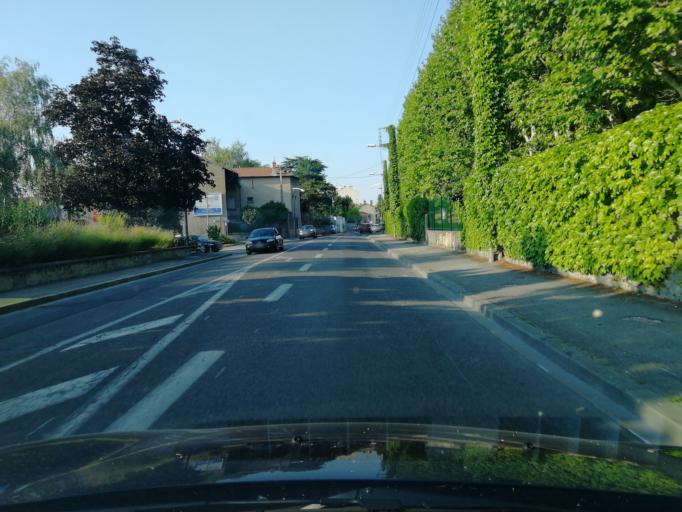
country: FR
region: Rhone-Alpes
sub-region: Departement du Rhone
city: Caluire-et-Cuire
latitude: 45.8055
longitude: 4.8538
